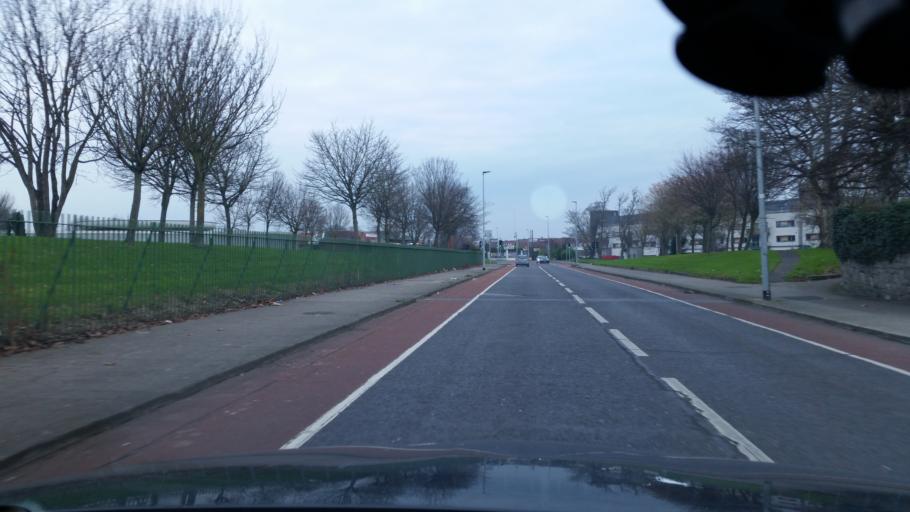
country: IE
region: Leinster
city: Artane
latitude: 53.3816
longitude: -6.2121
